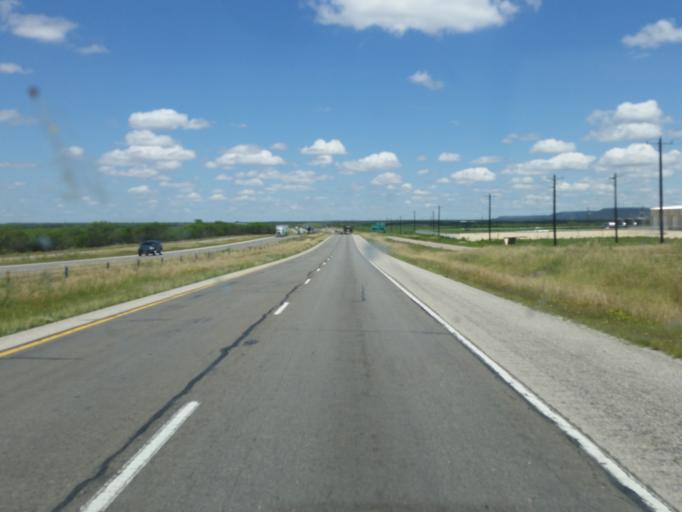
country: US
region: Texas
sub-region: Nolan County
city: Sweetwater
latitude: 32.4938
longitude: -100.2585
